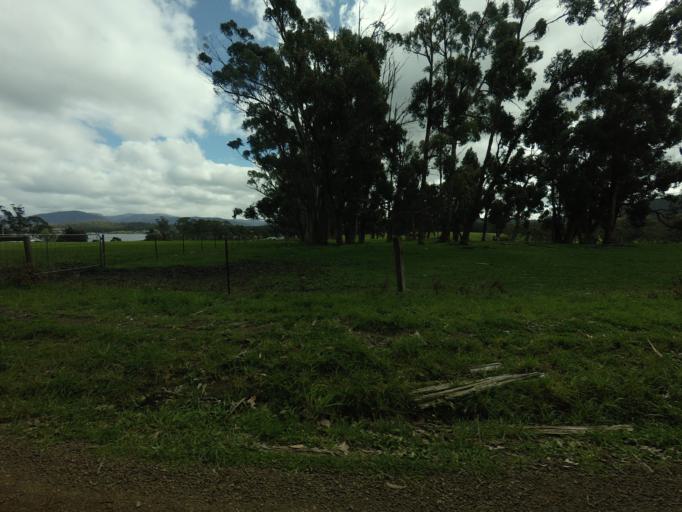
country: AU
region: Tasmania
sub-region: Huon Valley
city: Geeveston
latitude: -43.4350
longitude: 146.9867
